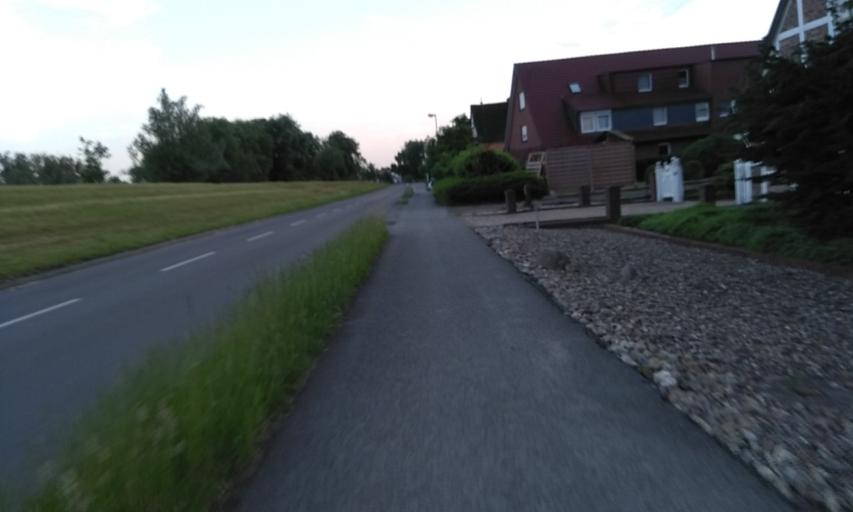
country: DE
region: Lower Saxony
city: Buxtehude
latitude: 53.4856
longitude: 9.7056
